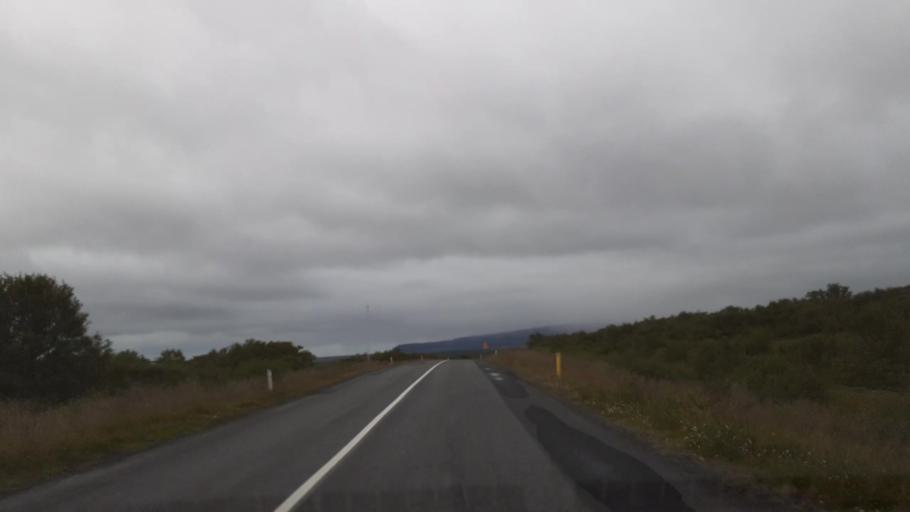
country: IS
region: Northeast
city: Husavik
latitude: 66.0602
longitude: -16.4447
